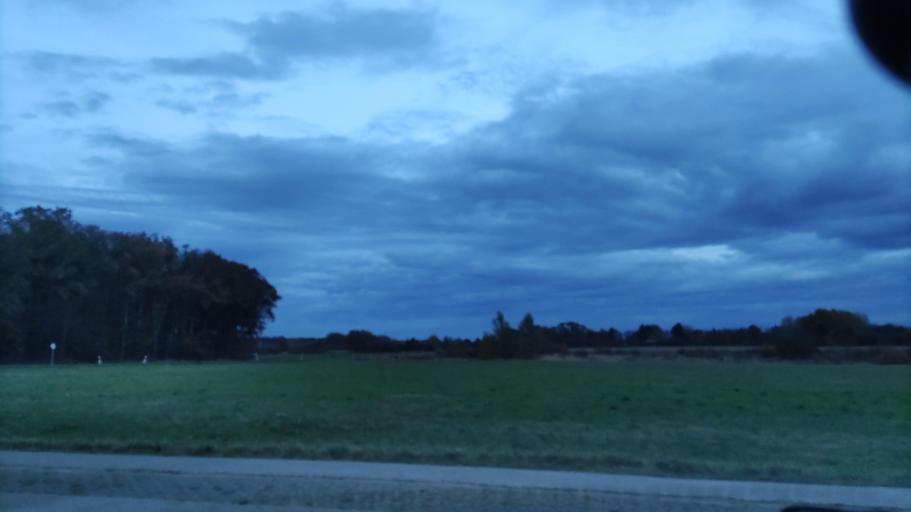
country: DE
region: Lower Saxony
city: Lehre
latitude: 52.2918
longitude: 10.6649
